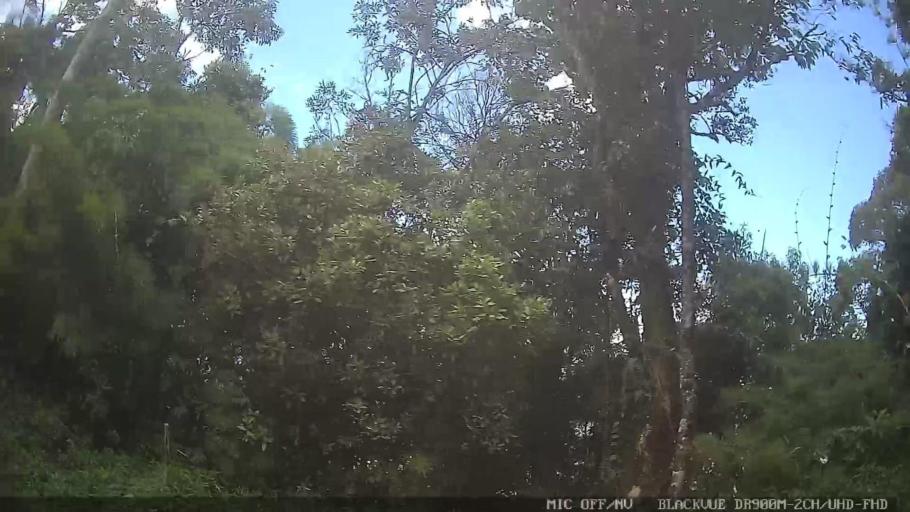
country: BR
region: Minas Gerais
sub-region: Extrema
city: Extrema
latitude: -22.8889
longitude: -46.3199
